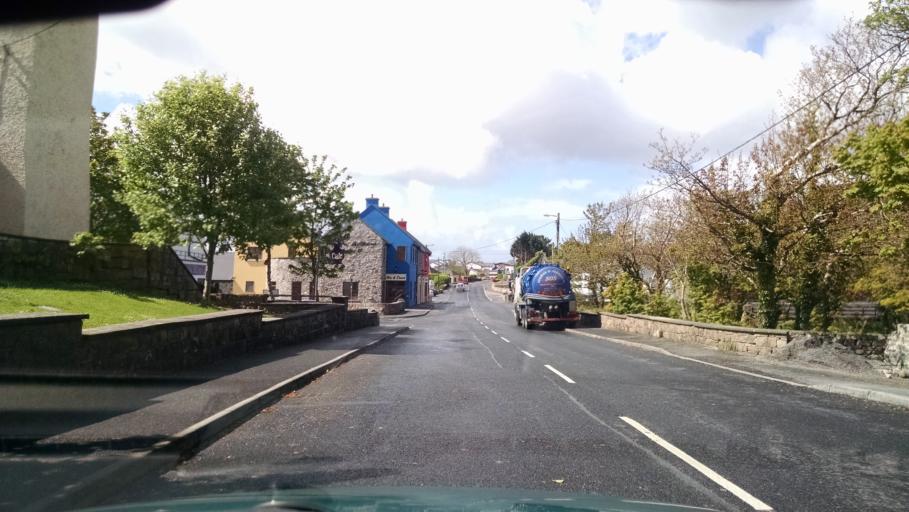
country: IE
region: Connaught
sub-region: County Galway
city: Oughterard
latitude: 53.2647
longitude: -9.5972
